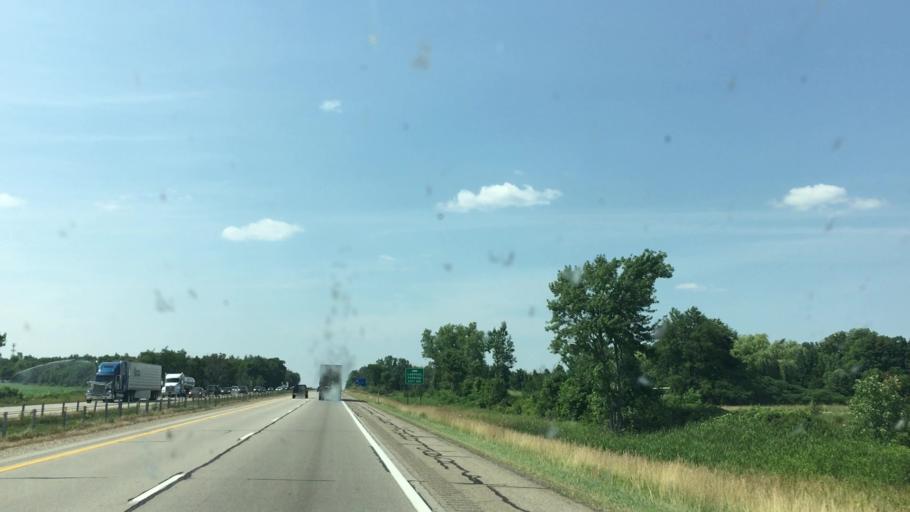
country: US
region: Michigan
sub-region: Allegan County
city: Wayland
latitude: 42.7137
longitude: -85.6639
